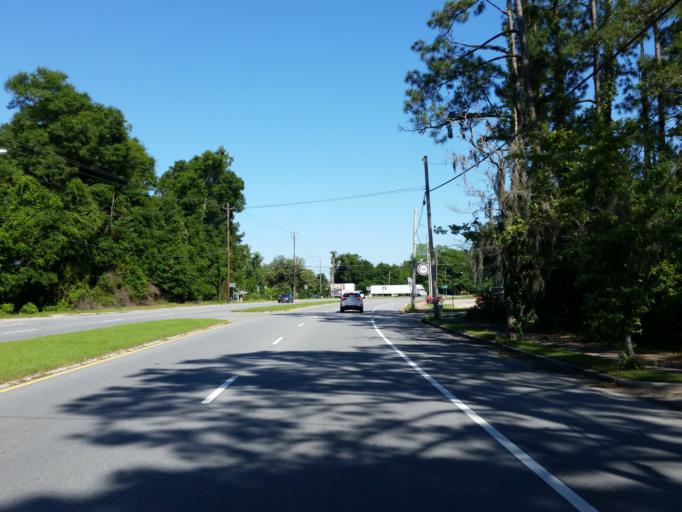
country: US
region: Georgia
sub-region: Echols County
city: Statenville
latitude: 30.6846
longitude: -83.1812
